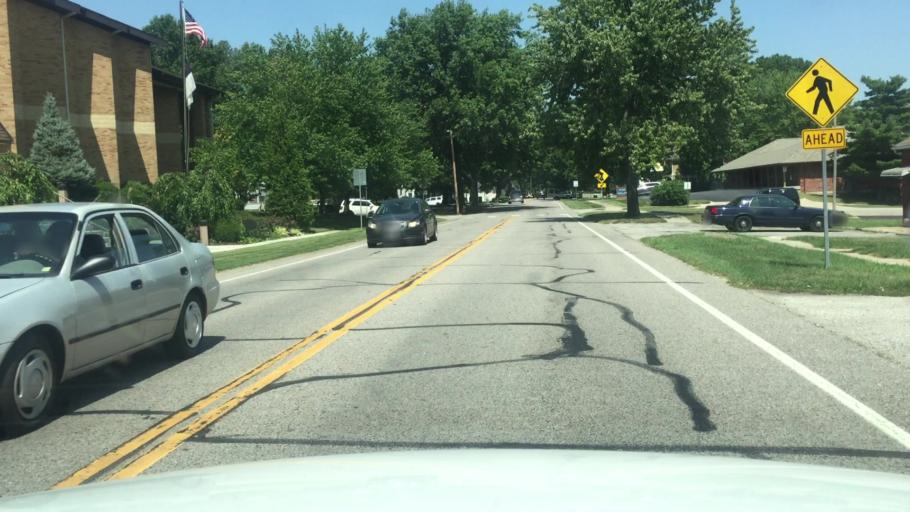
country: US
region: Missouri
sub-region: Jackson County
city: Lees Summit
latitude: 38.9159
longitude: -94.3786
